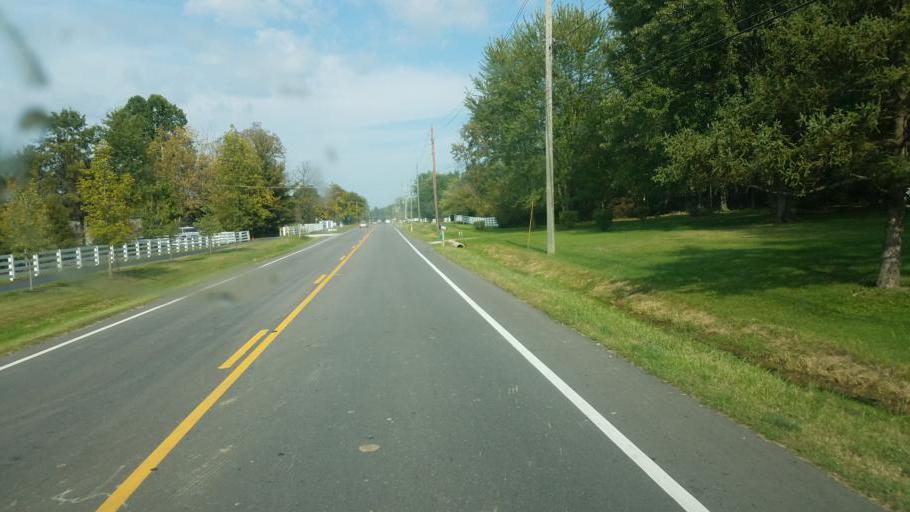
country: US
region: Ohio
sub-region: Franklin County
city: New Albany
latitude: 40.0584
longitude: -82.8361
